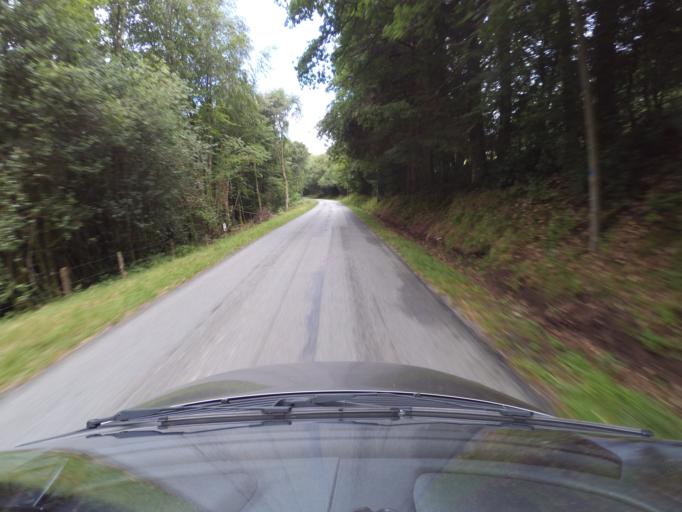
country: FR
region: Limousin
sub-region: Departement de la Correze
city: Bugeat
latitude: 45.7165
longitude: 2.0098
